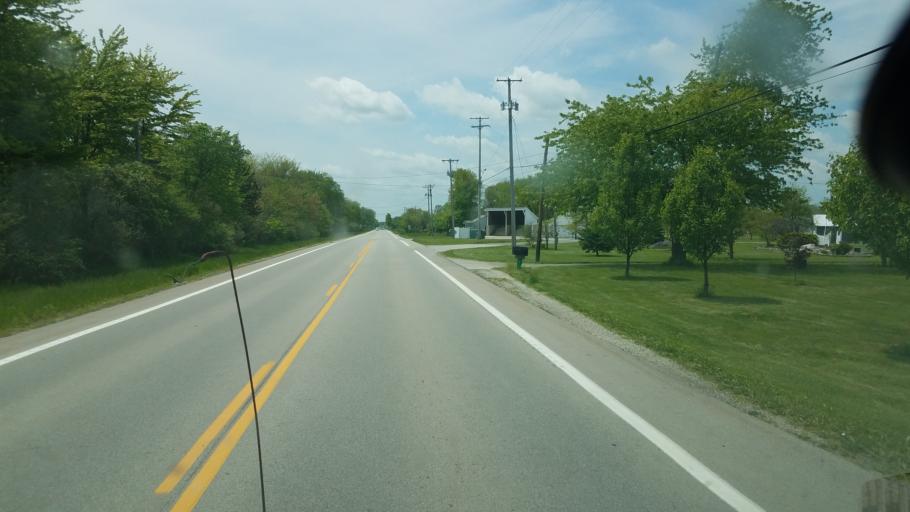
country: US
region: Ohio
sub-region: Ottawa County
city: Port Clinton
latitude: 41.4796
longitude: -83.0165
